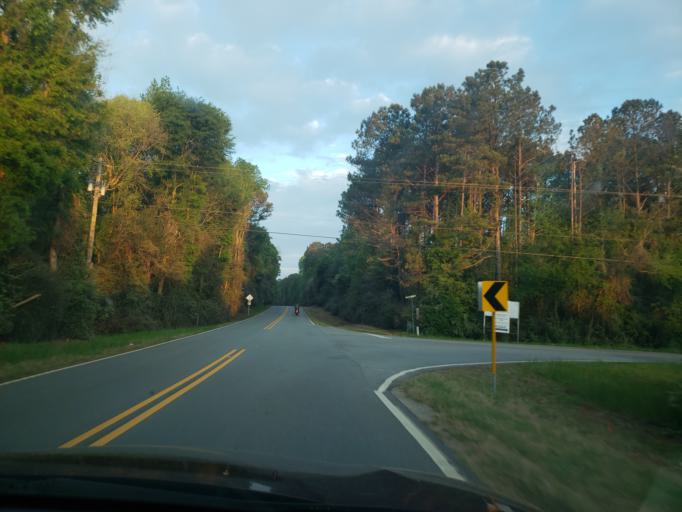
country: US
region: Alabama
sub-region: Tallapoosa County
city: Dadeville
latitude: 32.7103
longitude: -85.7739
